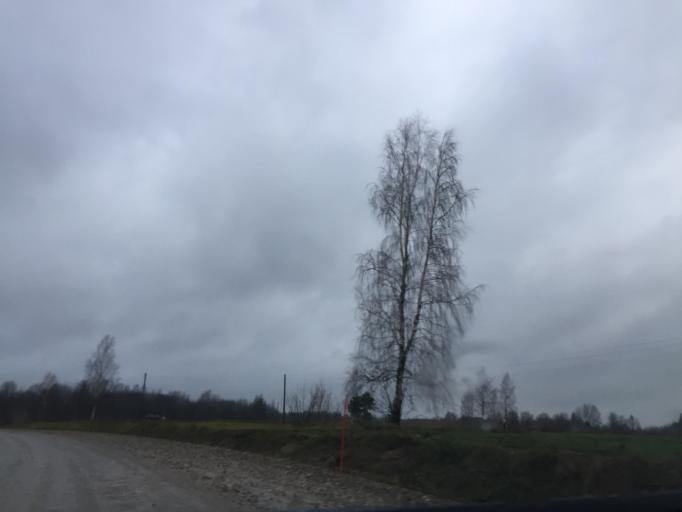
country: LV
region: Salacgrivas
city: Salacgriva
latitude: 57.7737
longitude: 24.5109
